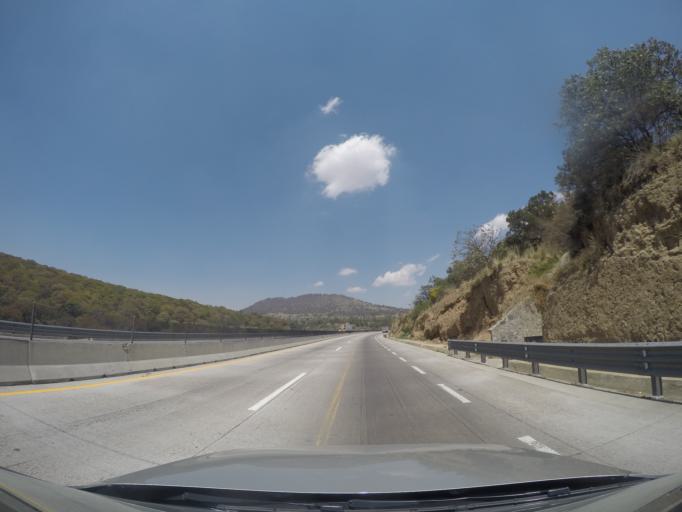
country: MX
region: Tlaxcala
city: Espanita
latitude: 19.4581
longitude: -98.4498
